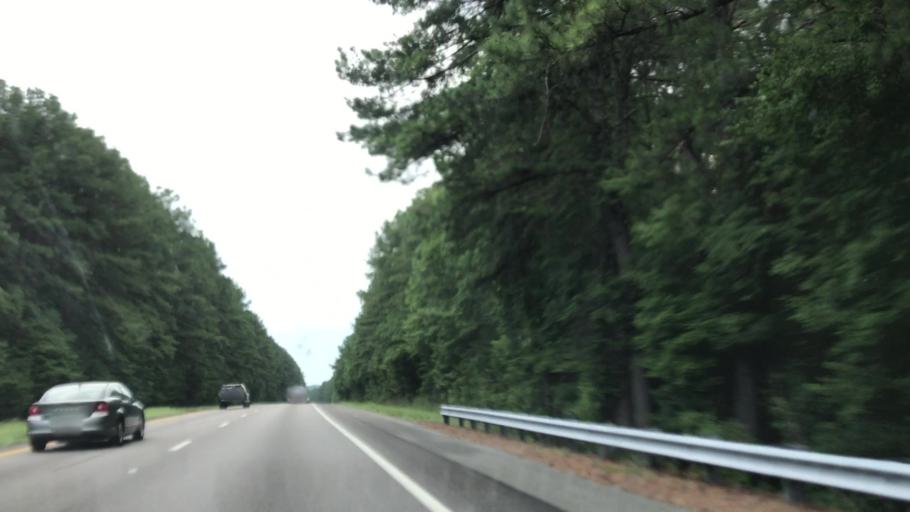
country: US
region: South Carolina
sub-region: Richland County
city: Blythewood
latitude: 34.2631
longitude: -80.9983
